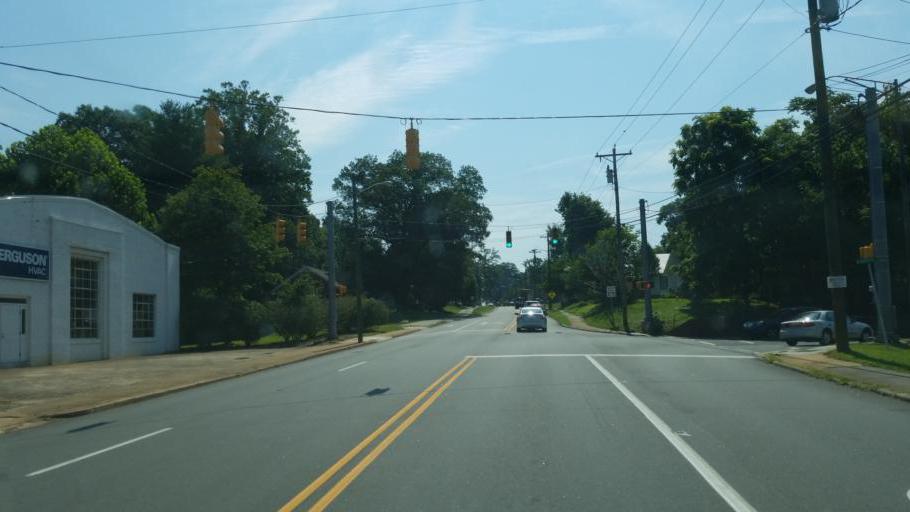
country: US
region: North Carolina
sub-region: Burke County
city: Morganton
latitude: 35.7488
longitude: -81.6982
